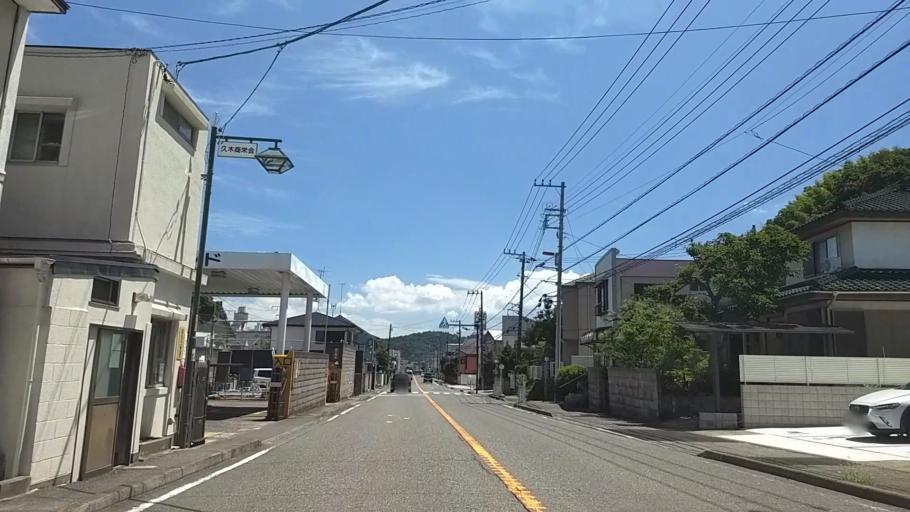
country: JP
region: Kanagawa
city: Zushi
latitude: 35.3043
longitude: 139.5694
